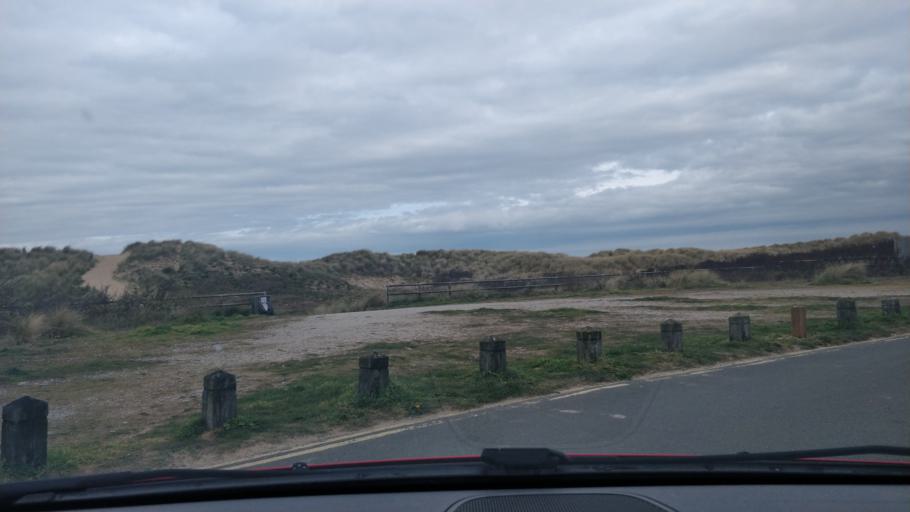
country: GB
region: England
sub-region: Sefton
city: Formby
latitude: 53.6058
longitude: -3.0629
